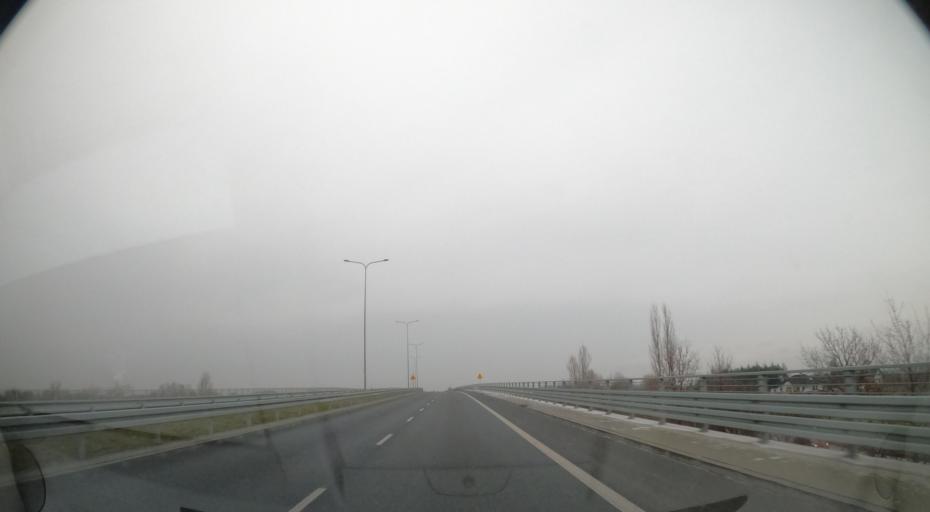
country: PL
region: Masovian Voivodeship
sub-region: Radom
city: Radom
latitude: 51.4069
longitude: 21.2026
